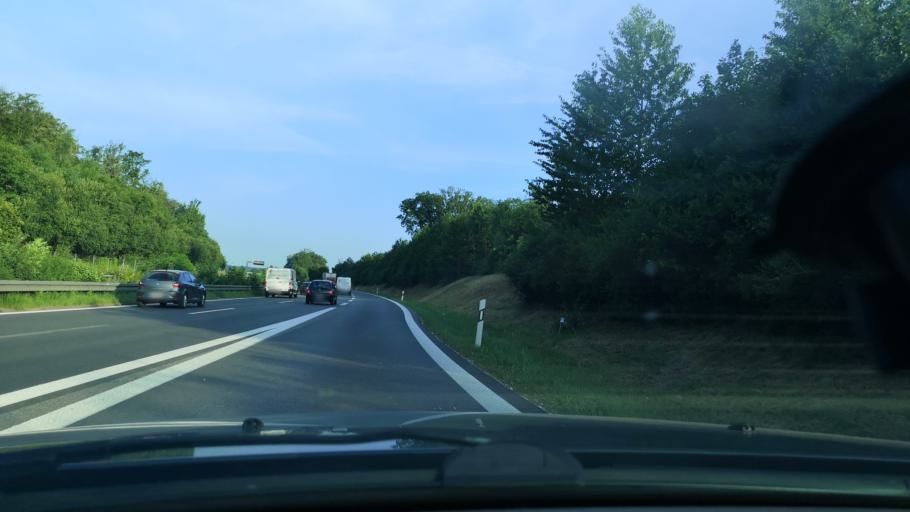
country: DE
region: Baden-Wuerttemberg
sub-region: Regierungsbezirk Stuttgart
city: Eislingen
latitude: 48.6805
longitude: 9.7194
